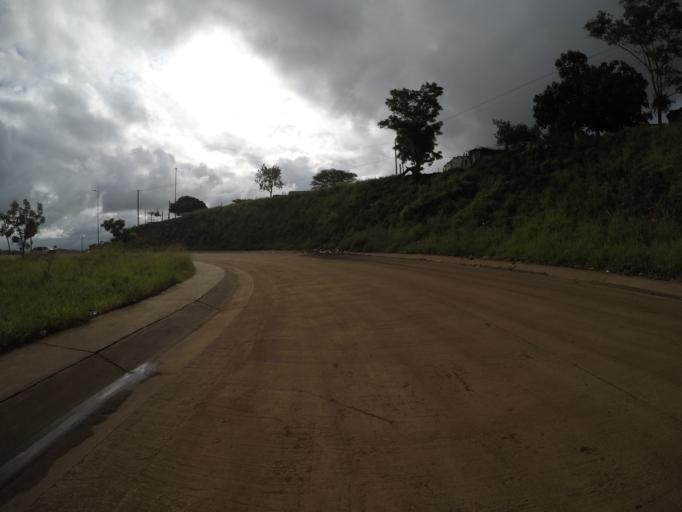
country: ZA
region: KwaZulu-Natal
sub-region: uMkhanyakude District Municipality
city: Mtubatuba
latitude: -28.4167
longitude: 32.1622
